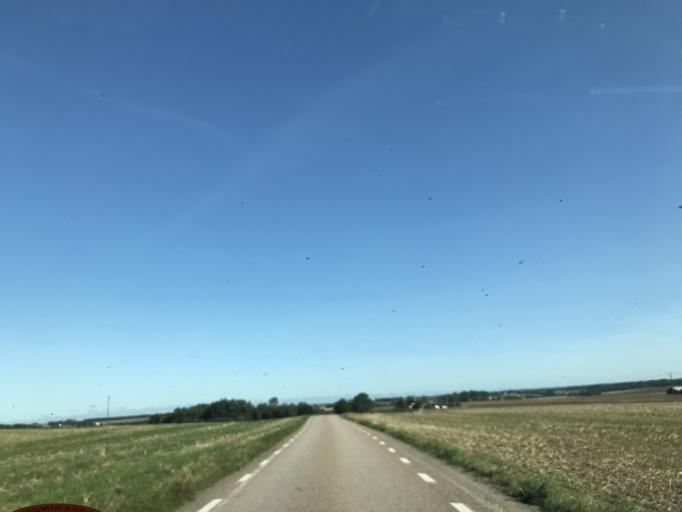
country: SE
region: Skane
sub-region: Landskrona
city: Asmundtorp
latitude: 55.9095
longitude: 12.9508
